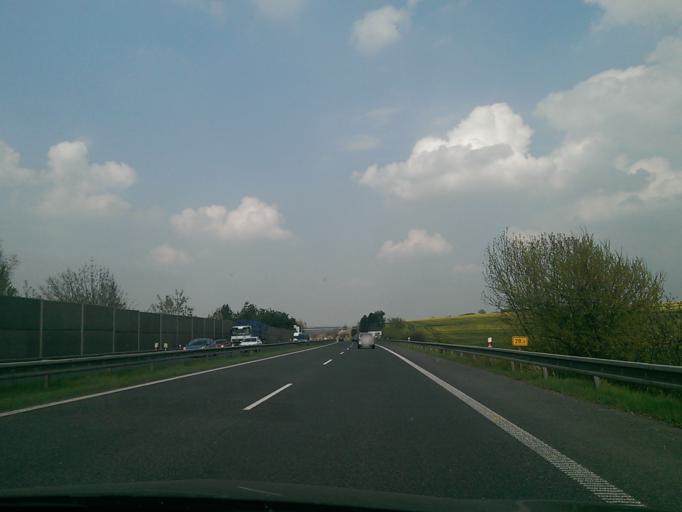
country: CZ
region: Central Bohemia
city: Benatky nad Jizerou
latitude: 50.2836
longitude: 14.8370
